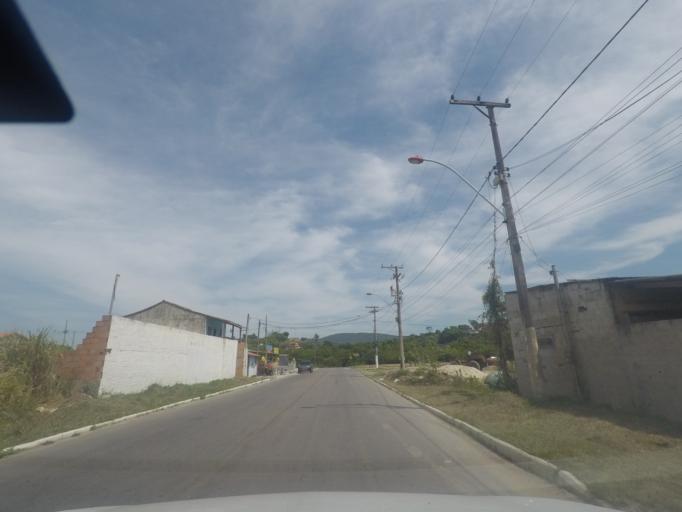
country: BR
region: Rio de Janeiro
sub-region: Marica
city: Marica
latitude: -22.9470
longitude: -42.7525
